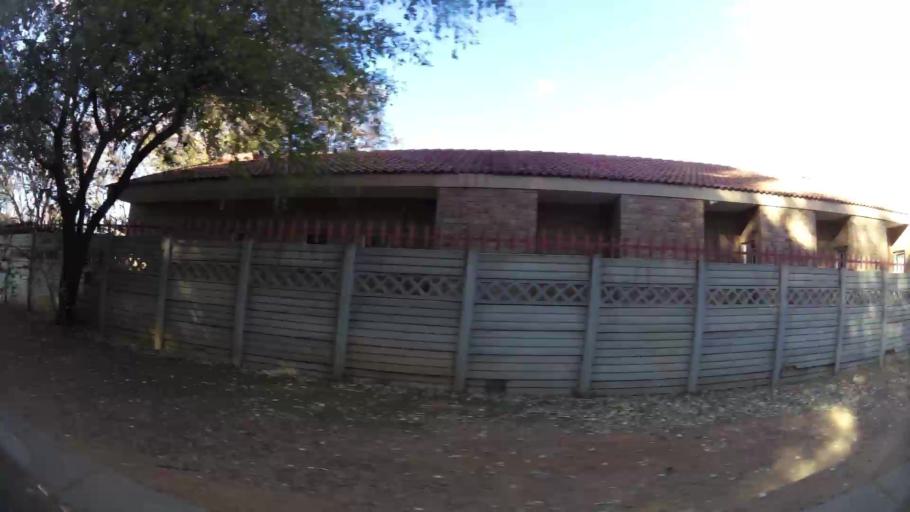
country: ZA
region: North-West
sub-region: Dr Kenneth Kaunda District Municipality
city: Klerksdorp
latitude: -26.8402
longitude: 26.6627
